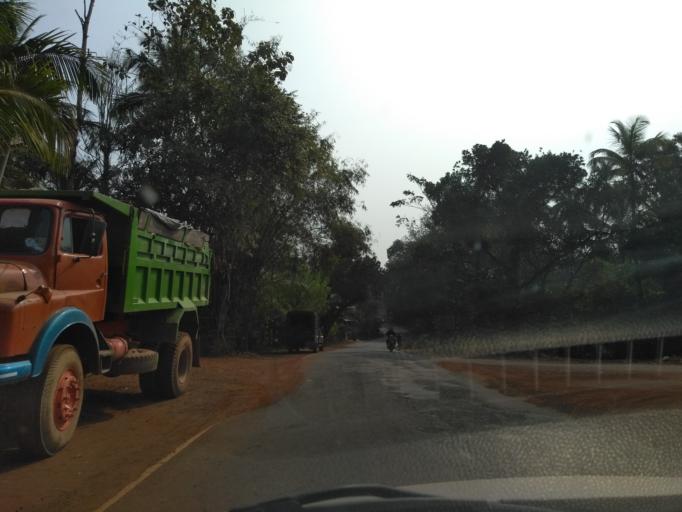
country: IN
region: Goa
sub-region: North Goa
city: Pernem
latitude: 15.7609
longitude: 73.9235
